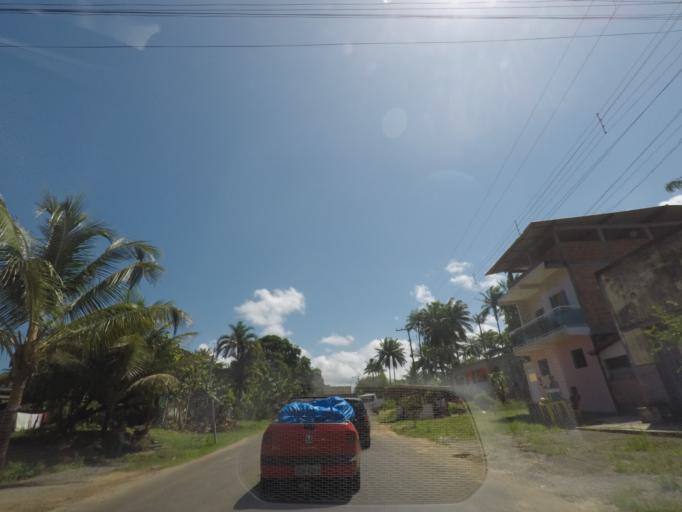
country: BR
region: Bahia
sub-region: Taperoa
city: Taperoa
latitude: -13.4578
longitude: -39.0885
